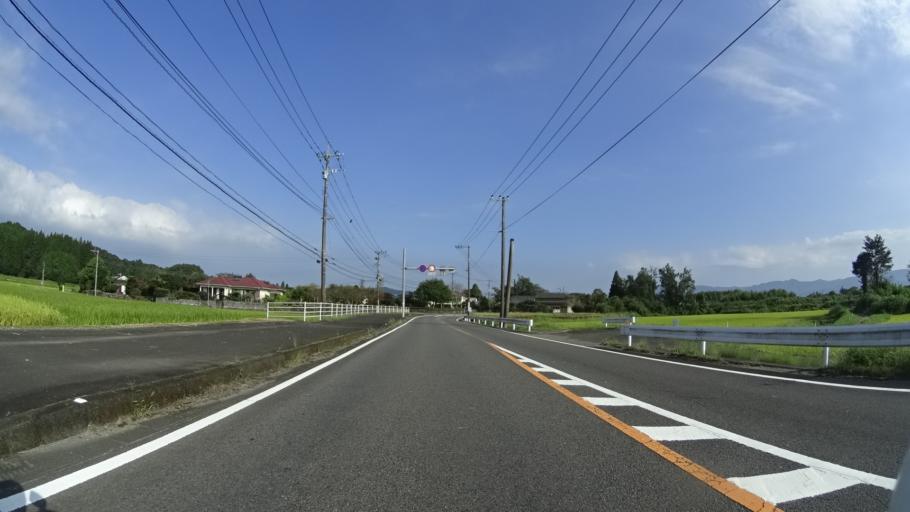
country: JP
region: Kagoshima
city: Okuchi-shinohara
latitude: 32.0251
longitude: 130.5957
